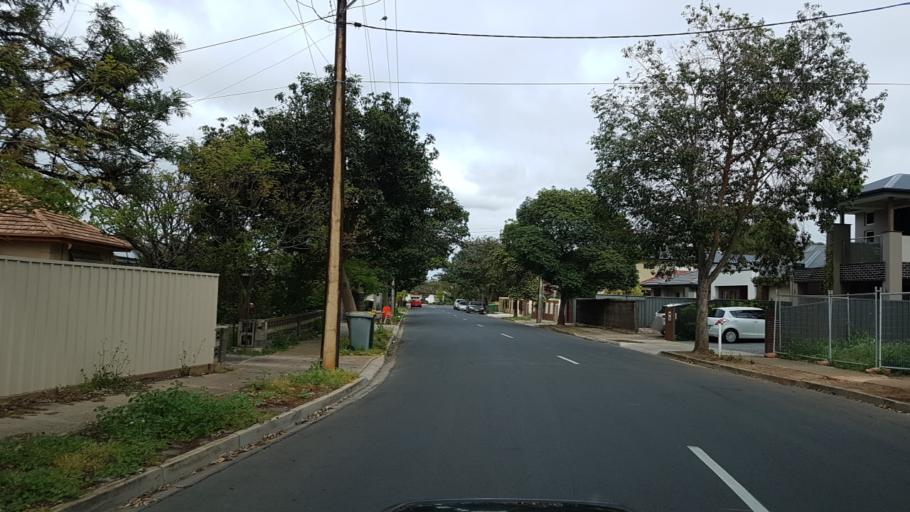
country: AU
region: South Australia
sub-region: Norwood Payneham St Peters
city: Marden
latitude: -34.8931
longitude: 138.6374
